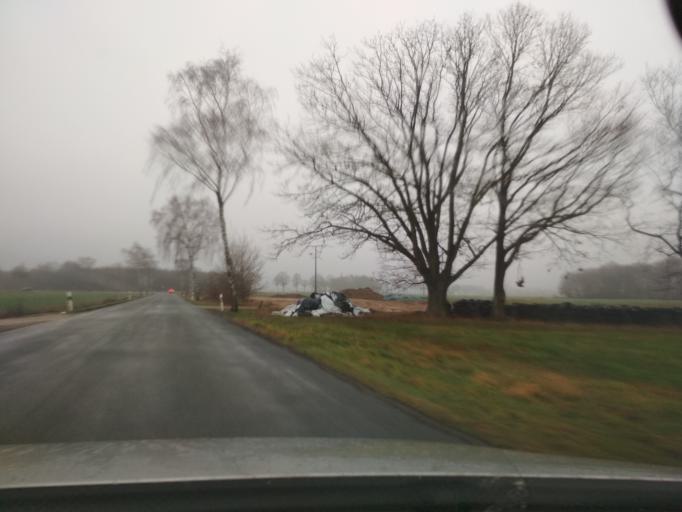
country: DE
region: Lower Saxony
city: Schoneworde
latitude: 52.6263
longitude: 10.6230
